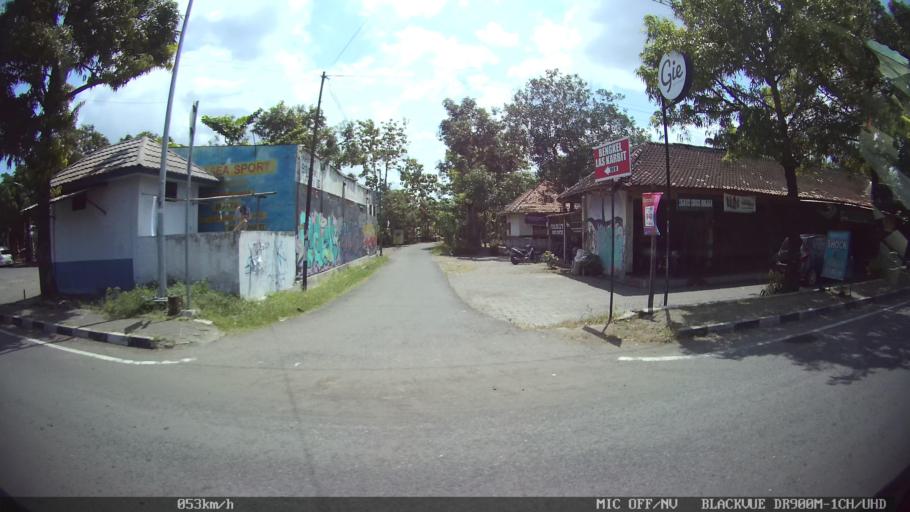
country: ID
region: Daerah Istimewa Yogyakarta
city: Bantul
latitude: -7.9054
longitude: 110.3191
